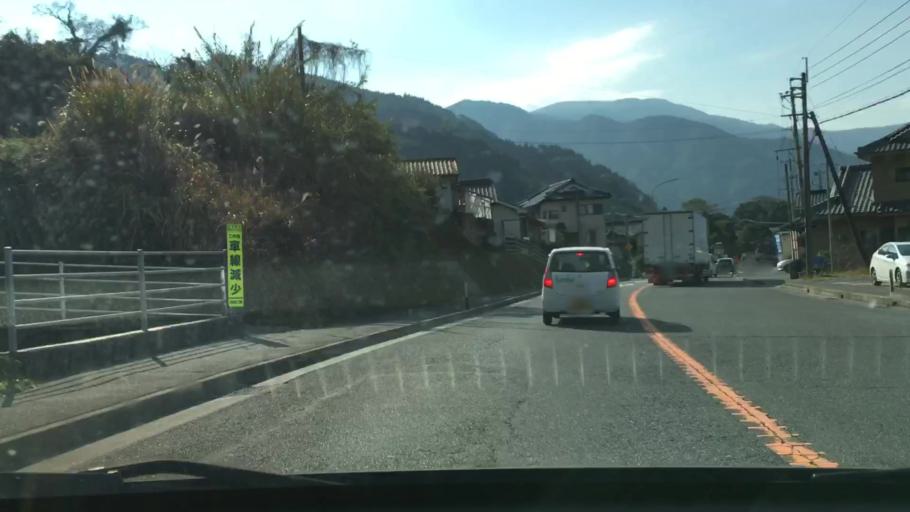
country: JP
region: Kagoshima
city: Hamanoichi
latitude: 31.5945
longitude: 130.7888
